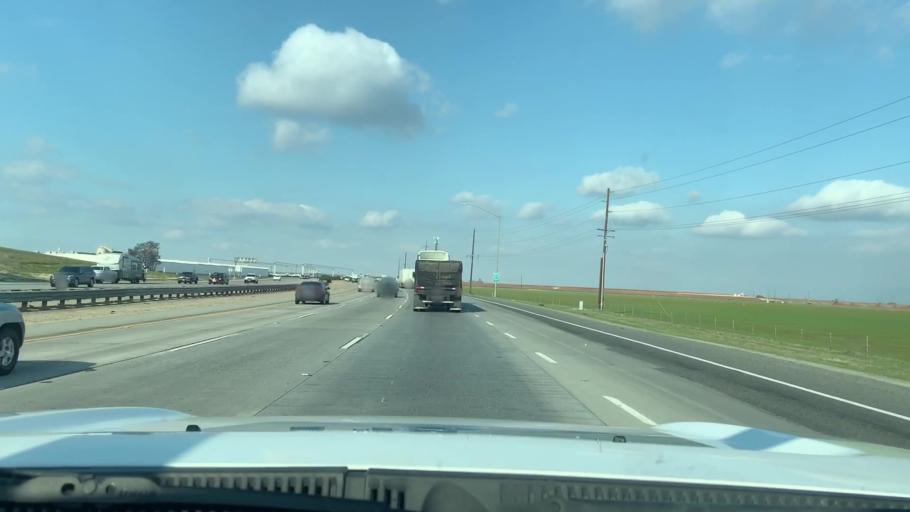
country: US
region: California
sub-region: Kern County
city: Shafter
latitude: 35.5590
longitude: -119.1973
